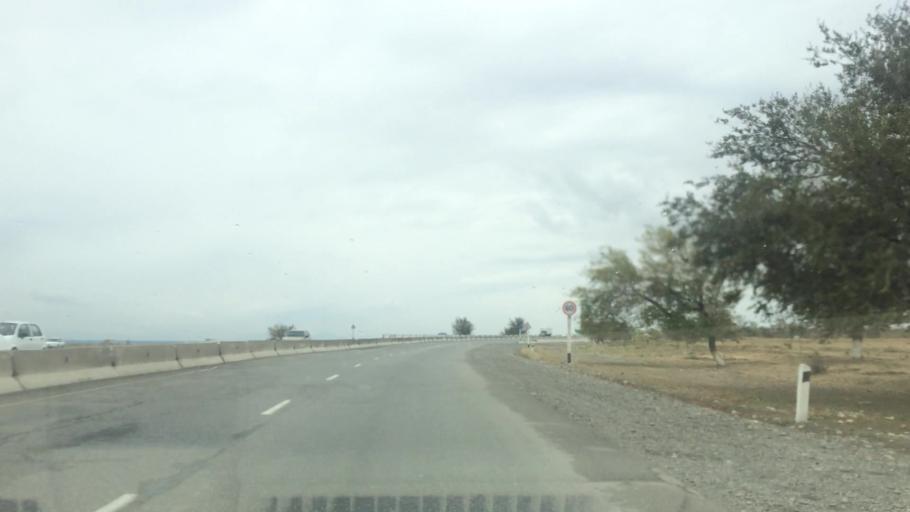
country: UZ
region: Samarqand
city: Bulung'ur
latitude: 39.8374
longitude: 67.4454
